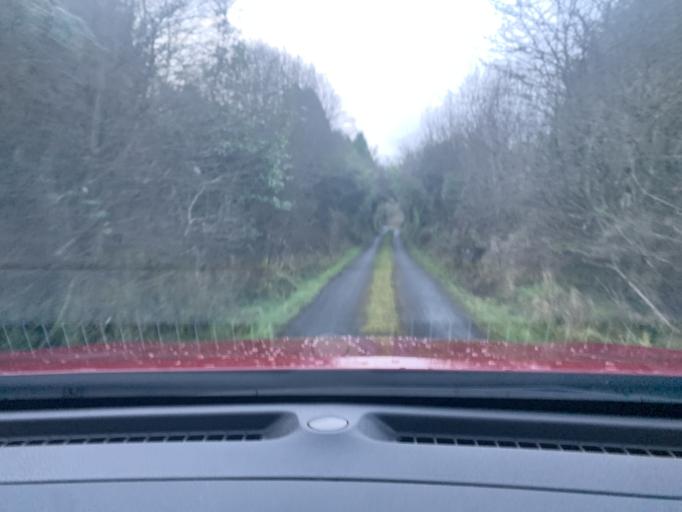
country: IE
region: Connaught
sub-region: Sligo
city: Ballymote
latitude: 53.9884
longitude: -8.4416
